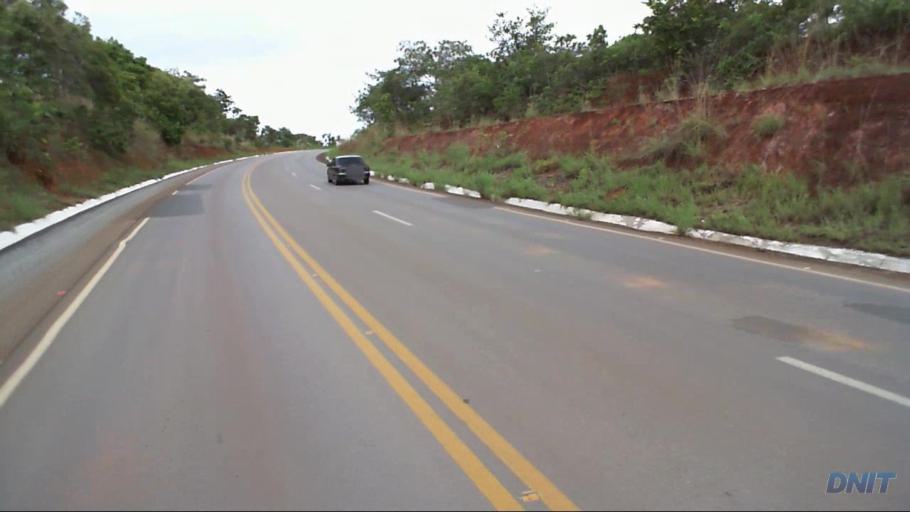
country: BR
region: Goias
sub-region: Barro Alto
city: Barro Alto
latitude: -14.8670
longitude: -49.0145
